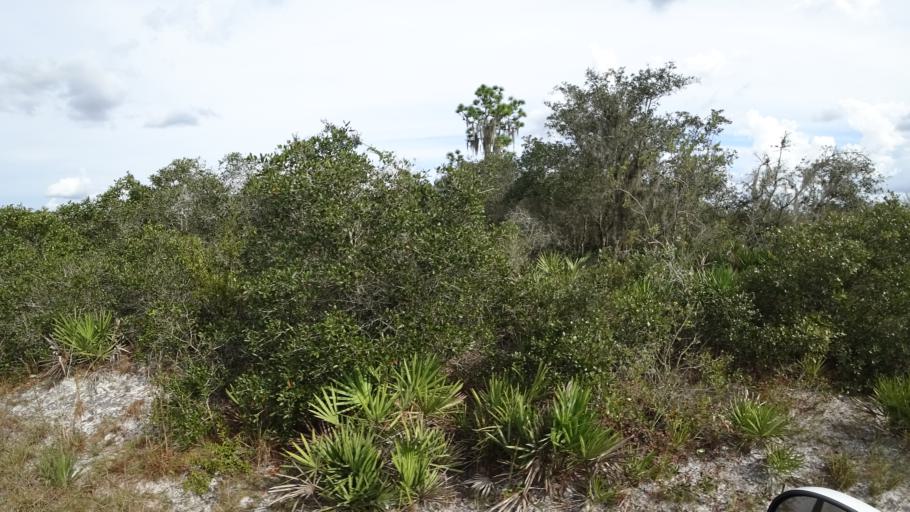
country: US
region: Florida
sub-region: Hillsborough County
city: Wimauma
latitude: 27.5589
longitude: -82.1432
